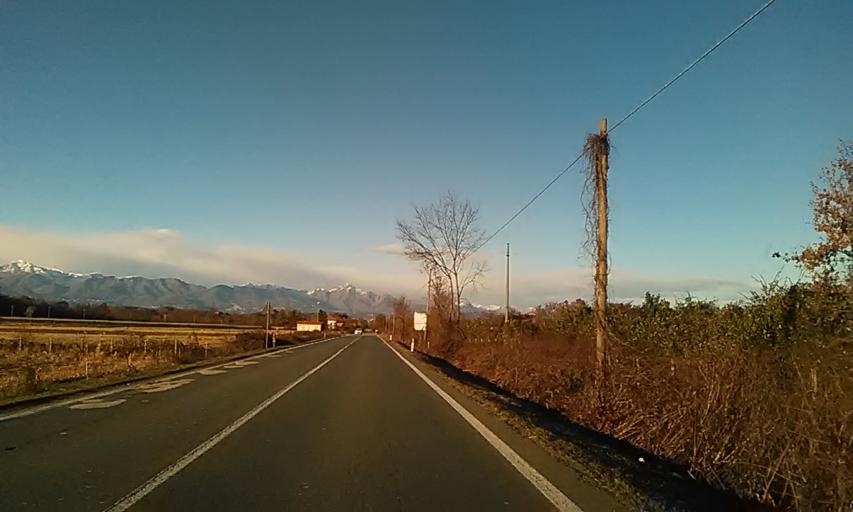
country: IT
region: Piedmont
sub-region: Provincia di Biella
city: Gifflenga
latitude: 45.4814
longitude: 8.2179
